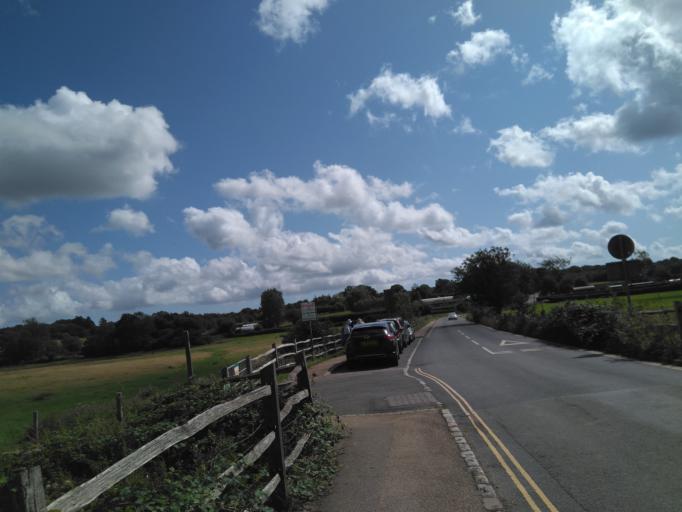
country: GB
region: England
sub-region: Kent
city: Hawkhurst
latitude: 50.9992
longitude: 0.5405
